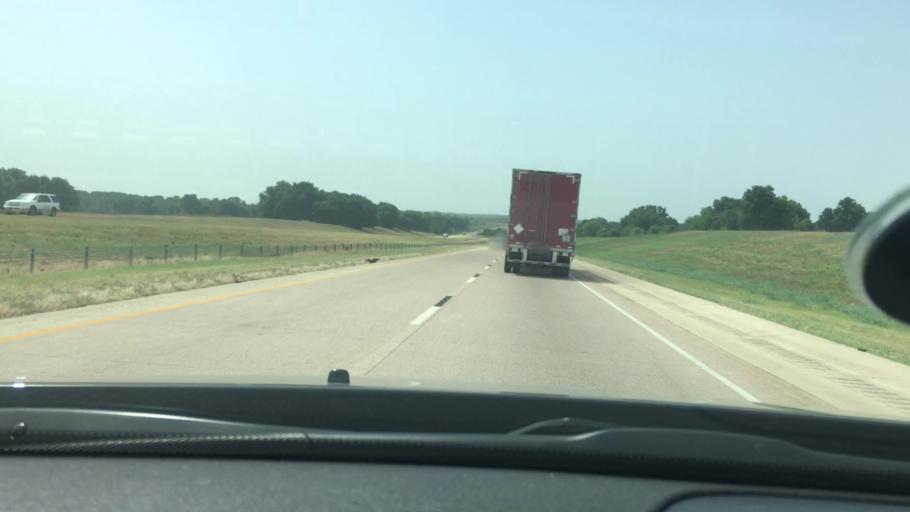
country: US
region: Oklahoma
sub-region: Garvin County
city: Wynnewood
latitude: 34.6723
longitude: -97.2254
